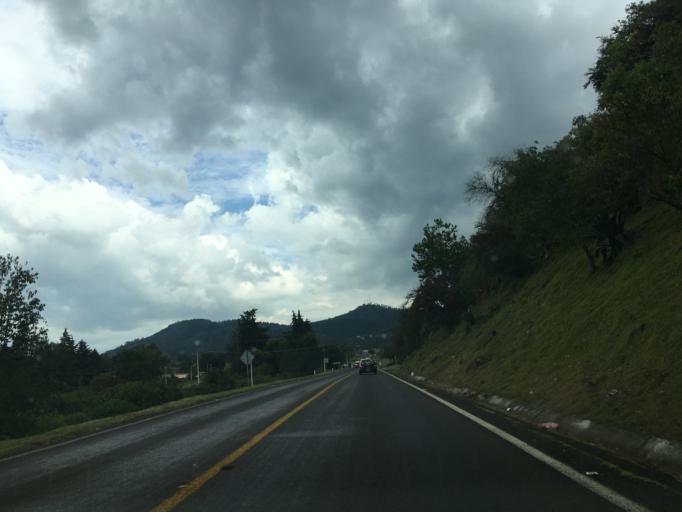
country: MX
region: Michoacan
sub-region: Patzcuaro
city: Santa Ana Chapitiro
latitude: 19.5329
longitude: -101.6327
